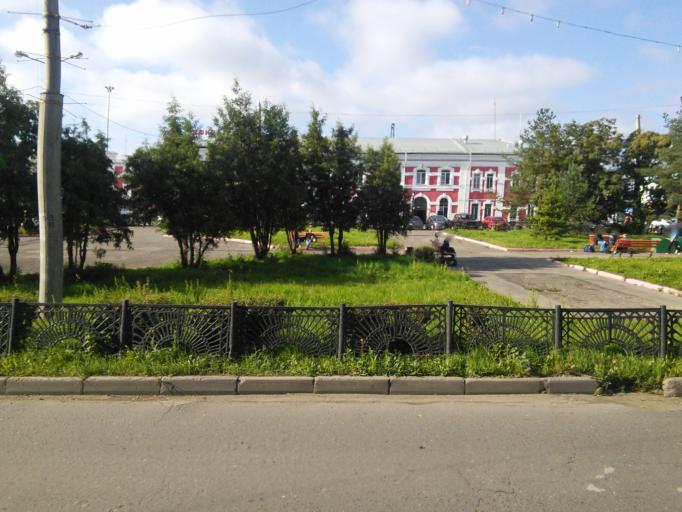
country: RU
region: Vologda
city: Vologda
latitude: 59.2076
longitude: 39.8831
